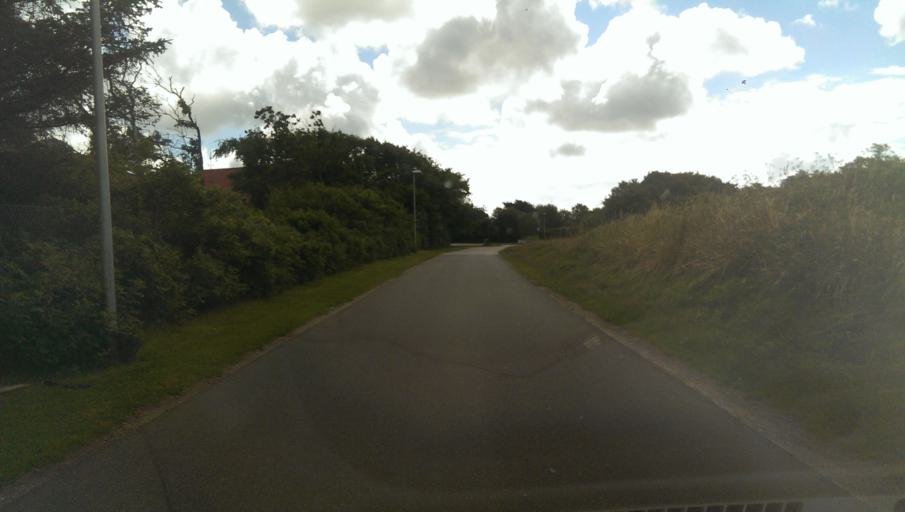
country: DK
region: Central Jutland
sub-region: Holstebro Kommune
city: Ulfborg
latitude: 56.2672
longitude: 8.2474
